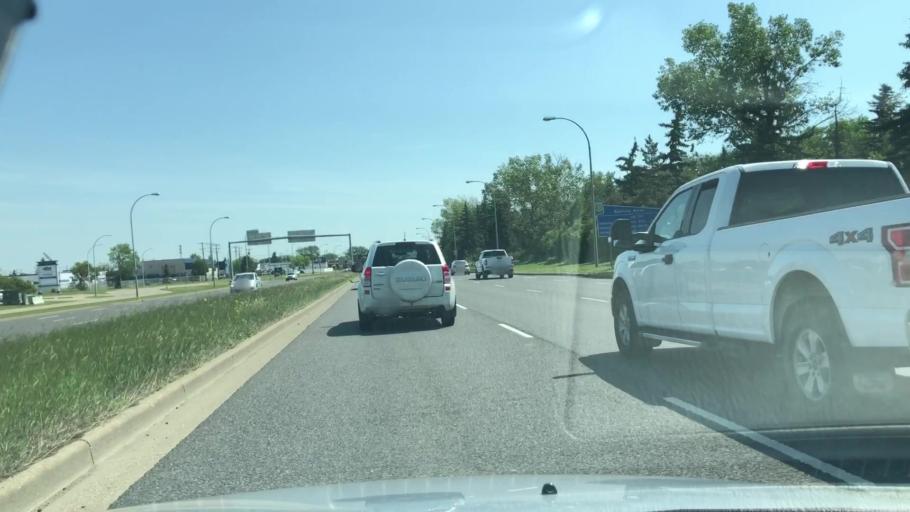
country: CA
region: Alberta
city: Edmonton
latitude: 53.5807
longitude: -113.5503
